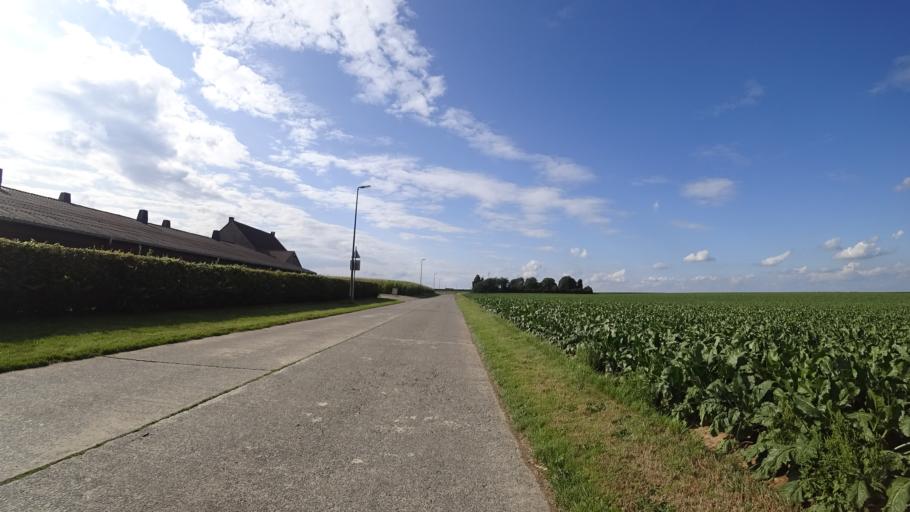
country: BE
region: Wallonia
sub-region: Province du Brabant Wallon
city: Chastre
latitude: 50.5717
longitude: 4.6221
